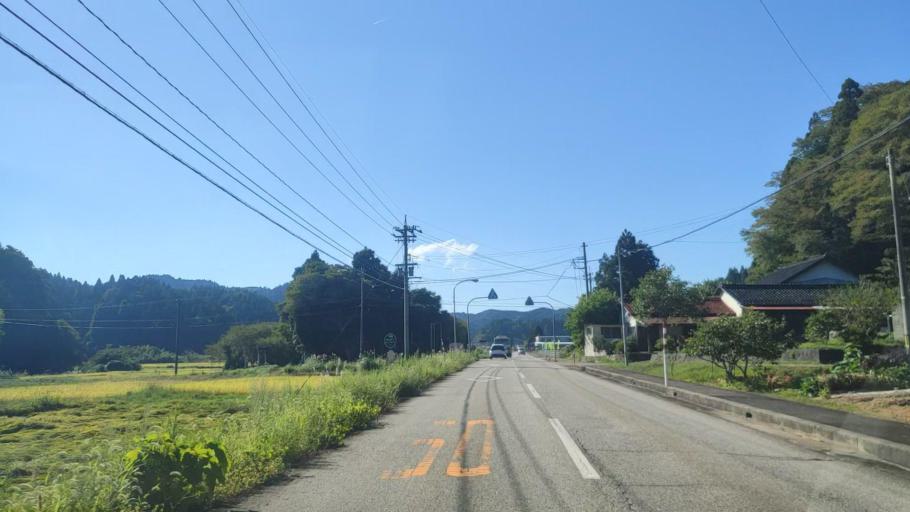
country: JP
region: Ishikawa
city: Nanao
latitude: 37.2790
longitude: 137.0494
